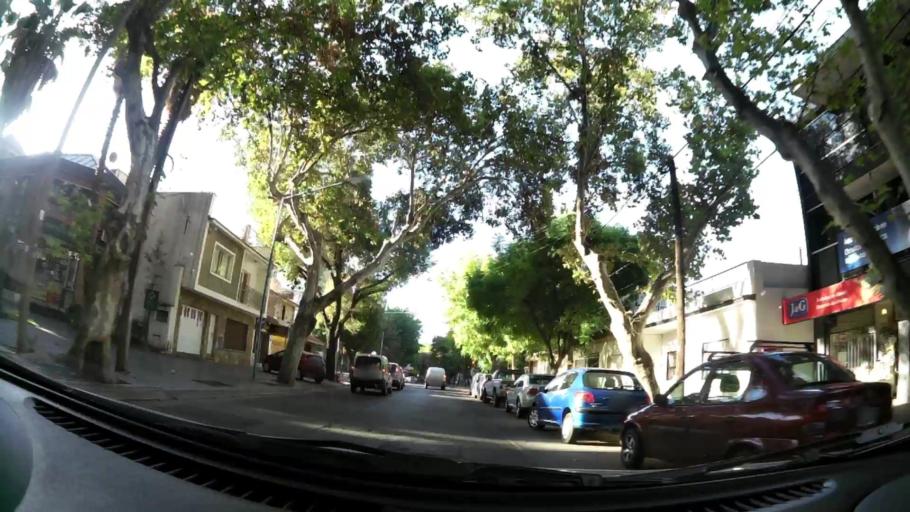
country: AR
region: Mendoza
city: Mendoza
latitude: -32.9052
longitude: -68.8516
